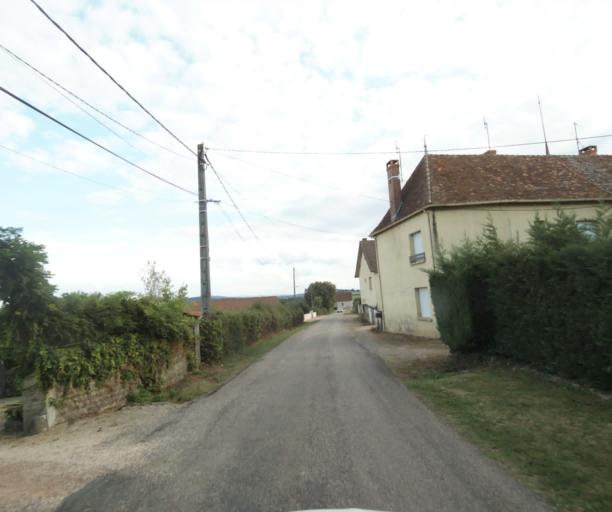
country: FR
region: Bourgogne
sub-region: Departement de Saone-et-Loire
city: Charolles
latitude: 46.4469
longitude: 4.3304
